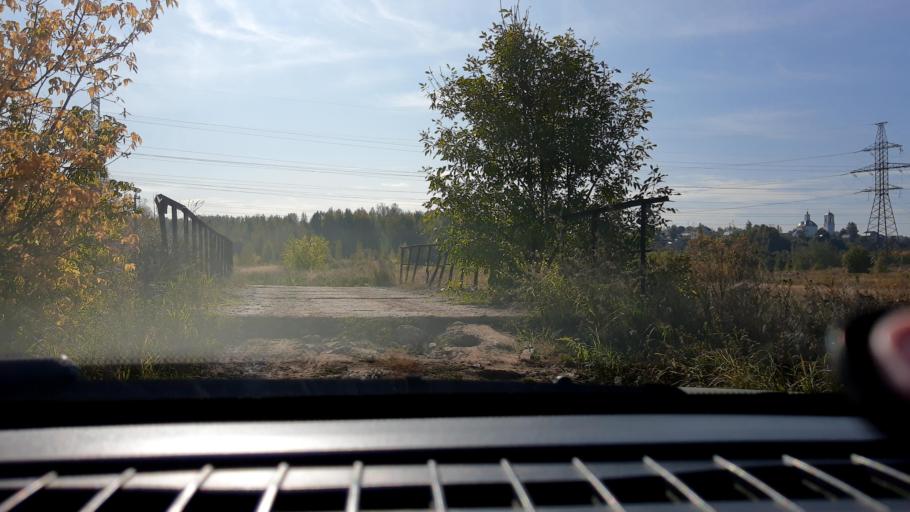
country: RU
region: Nizjnij Novgorod
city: Afonino
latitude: 56.2376
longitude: 44.0597
